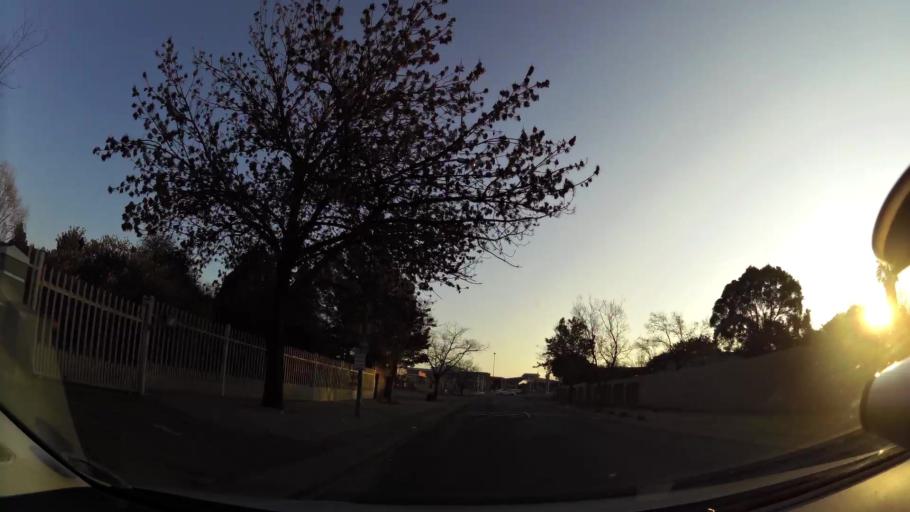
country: ZA
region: Orange Free State
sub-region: Mangaung Metropolitan Municipality
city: Bloemfontein
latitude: -29.1022
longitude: 26.1587
